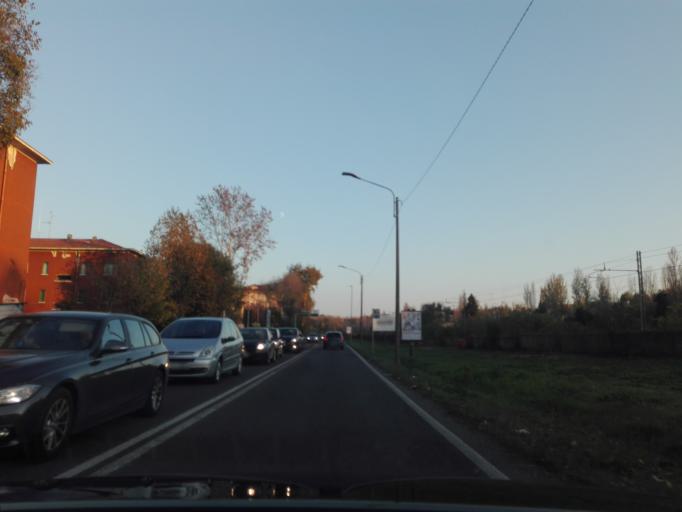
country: IT
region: Lombardy
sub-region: Provincia di Mantova
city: Mantova
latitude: 45.1444
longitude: 10.7962
